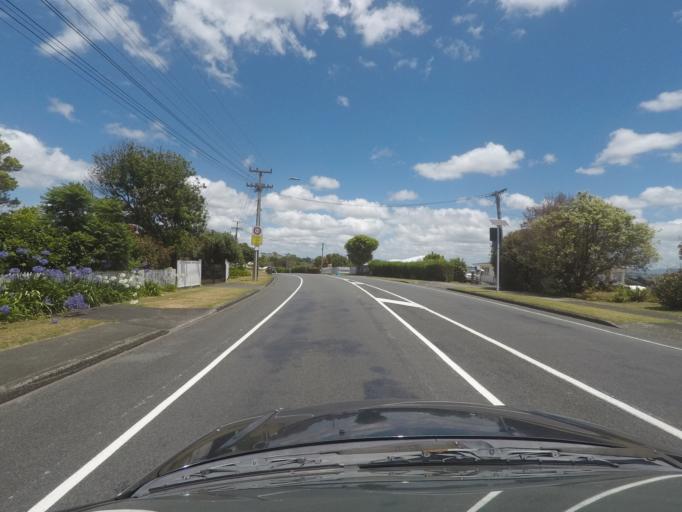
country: NZ
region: Northland
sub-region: Whangarei
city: Whangarei
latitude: -35.7596
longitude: 174.3672
